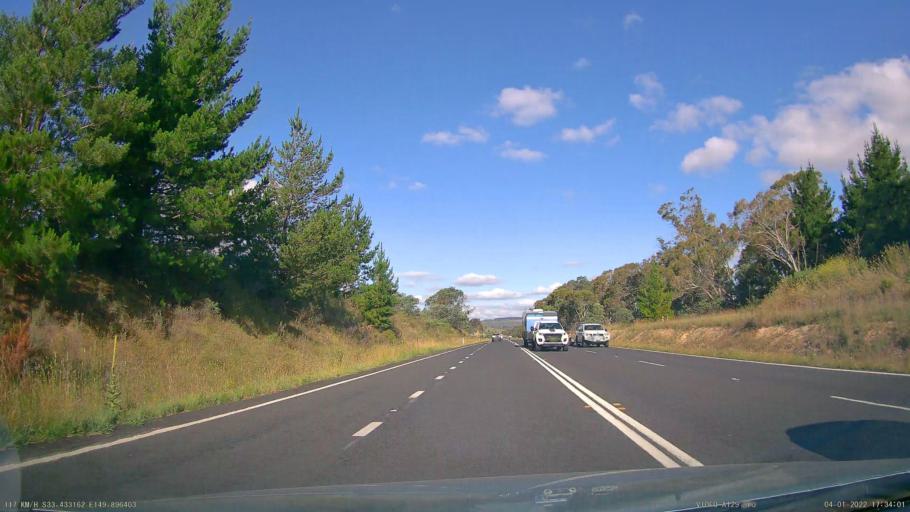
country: AU
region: New South Wales
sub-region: Lithgow
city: Portland
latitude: -33.4332
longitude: 149.8967
